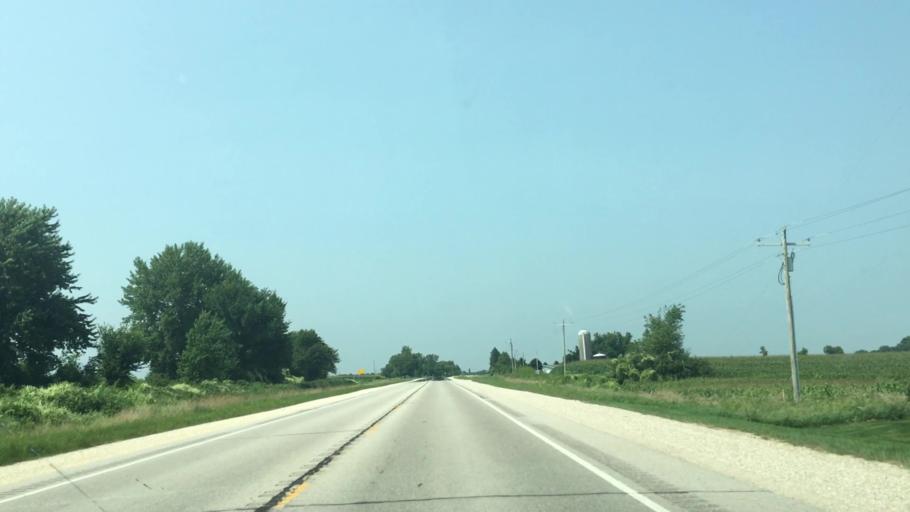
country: US
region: Iowa
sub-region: Winneshiek County
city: Decorah
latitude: 43.1996
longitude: -91.8754
